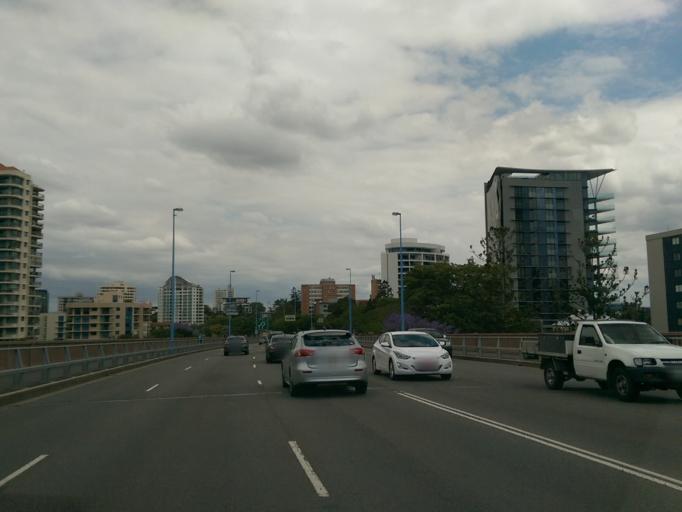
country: AU
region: Queensland
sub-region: Brisbane
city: Brisbane
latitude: -27.4690
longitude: 153.0359
